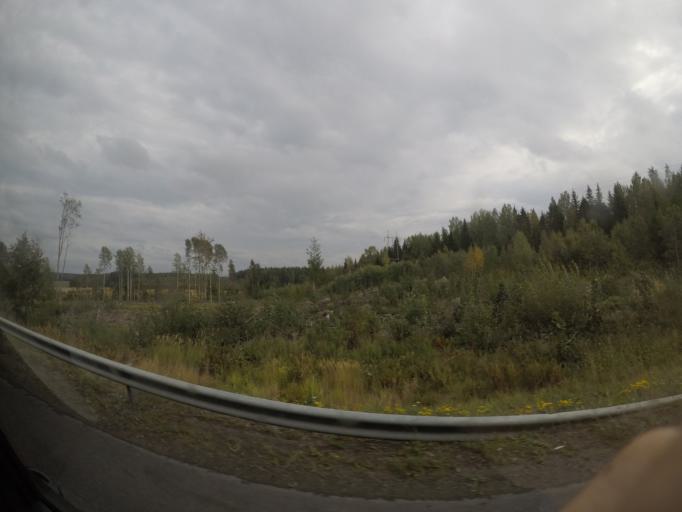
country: FI
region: Haeme
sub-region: Haemeenlinna
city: Parola
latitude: 61.0895
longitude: 24.4011
